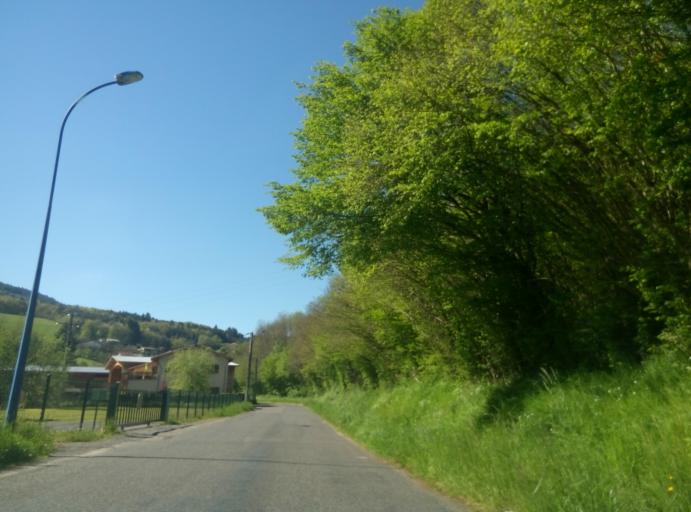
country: FR
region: Rhone-Alpes
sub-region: Departement du Rhone
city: Grandris
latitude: 46.0572
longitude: 4.4937
